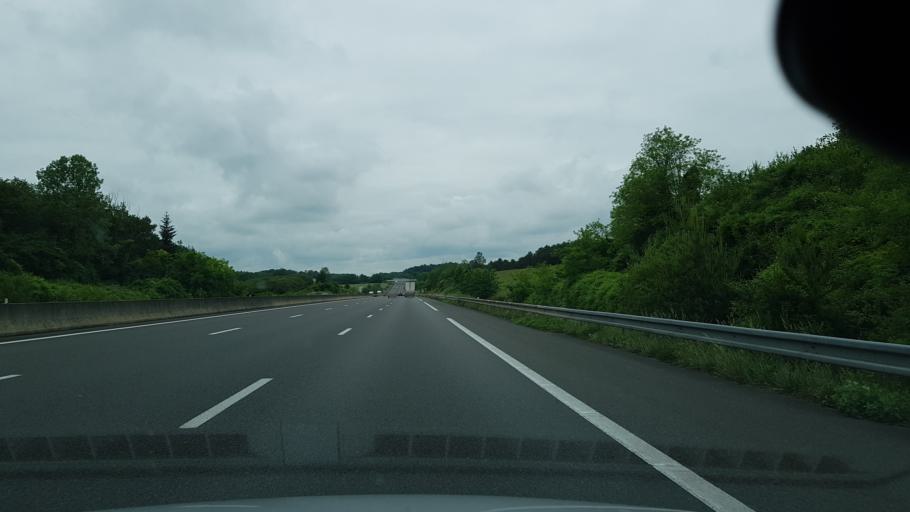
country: FR
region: Centre
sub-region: Departement du Loir-et-Cher
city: Saint-Sulpice-de-Pommeray
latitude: 47.6180
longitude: 1.2633
